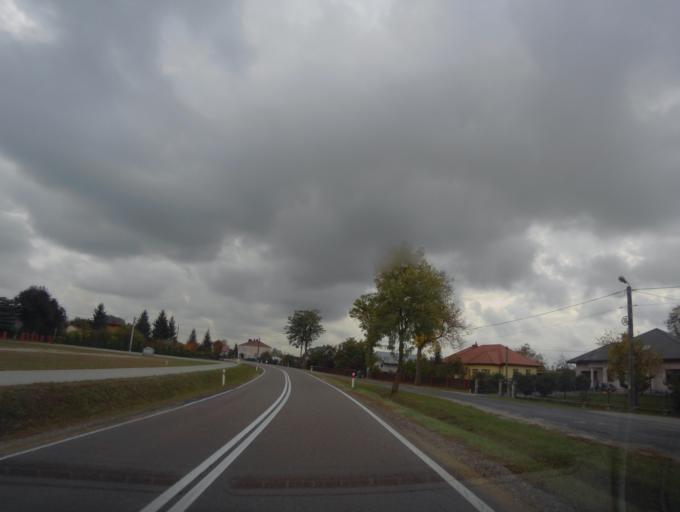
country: PL
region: Subcarpathian Voivodeship
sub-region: Powiat nizanski
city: Krzeszow
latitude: 50.3700
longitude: 22.3151
